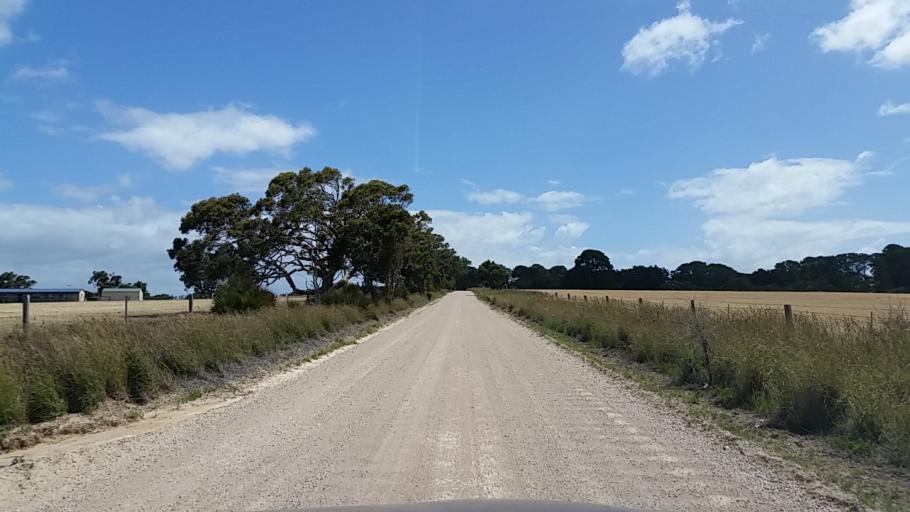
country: AU
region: South Australia
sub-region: Alexandrina
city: Port Elliot
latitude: -35.4505
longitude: 138.6479
